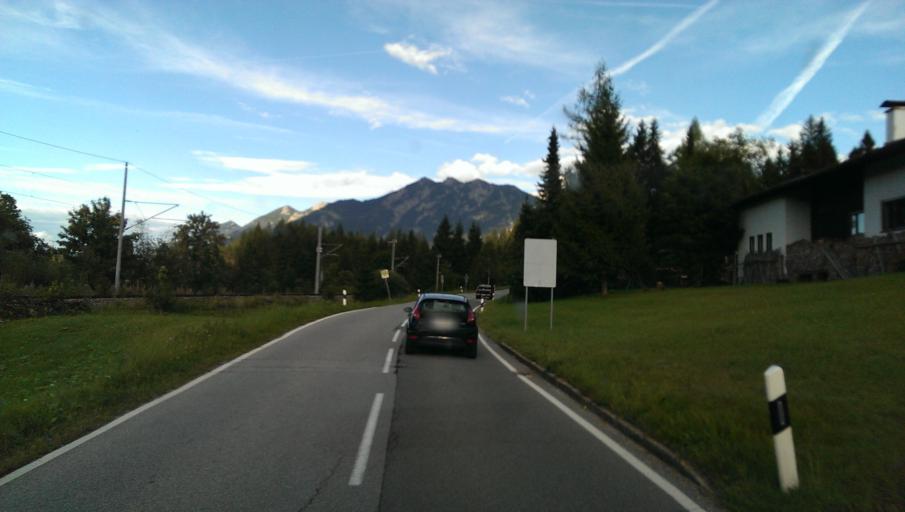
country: DE
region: Bavaria
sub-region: Upper Bavaria
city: Mittenwald
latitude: 47.4822
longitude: 11.2414
